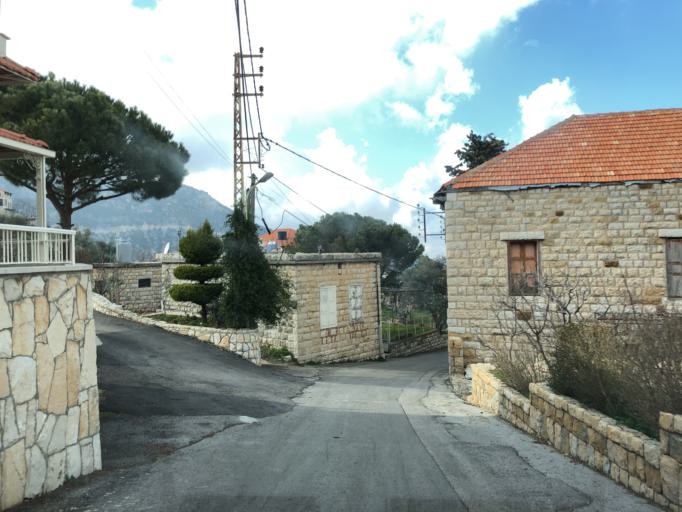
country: LB
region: Liban-Nord
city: Amioun
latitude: 34.2054
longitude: 35.8420
